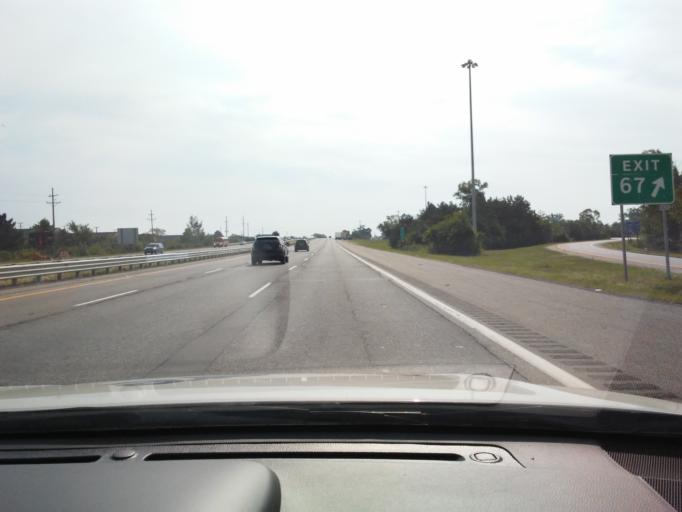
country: US
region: Michigan
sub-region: Oakland County
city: Clawson
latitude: 42.5592
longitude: -83.1356
